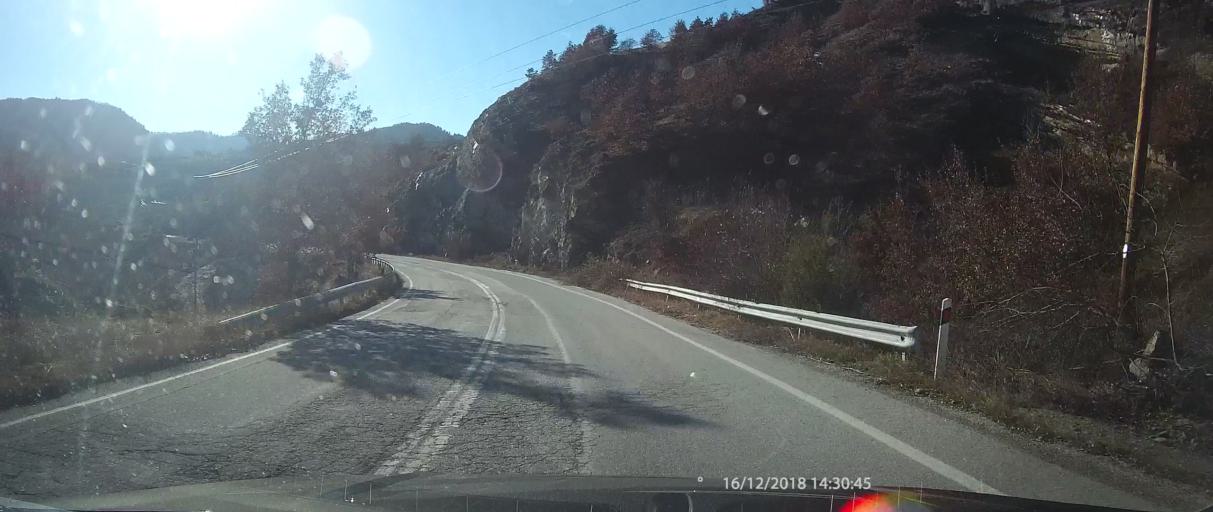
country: GR
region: West Macedonia
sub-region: Nomos Kozanis
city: Tsotili
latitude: 40.1954
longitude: 21.1878
